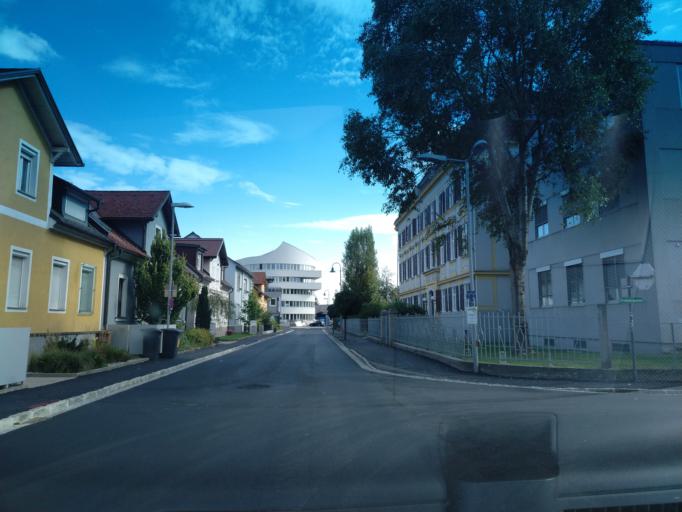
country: AT
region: Styria
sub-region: Politischer Bezirk Leibnitz
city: Leibnitz
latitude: 46.7792
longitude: 15.5384
